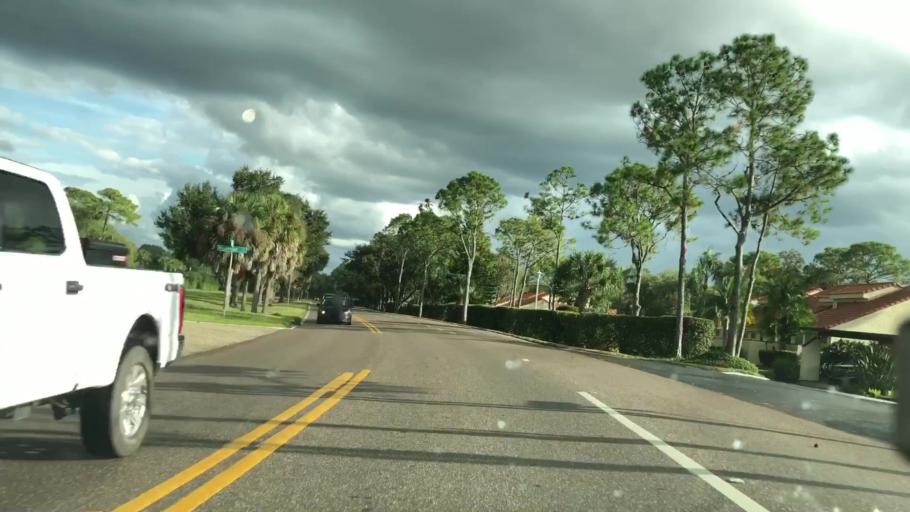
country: US
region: Florida
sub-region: Sarasota County
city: The Meadows
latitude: 27.3721
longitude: -82.4631
